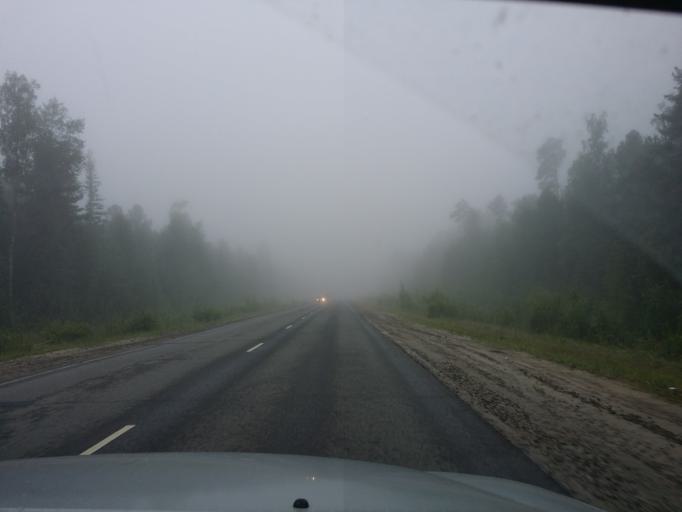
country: RU
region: Khanty-Mansiyskiy Avtonomnyy Okrug
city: Gornopravdinsk
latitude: 59.6740
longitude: 70.0274
